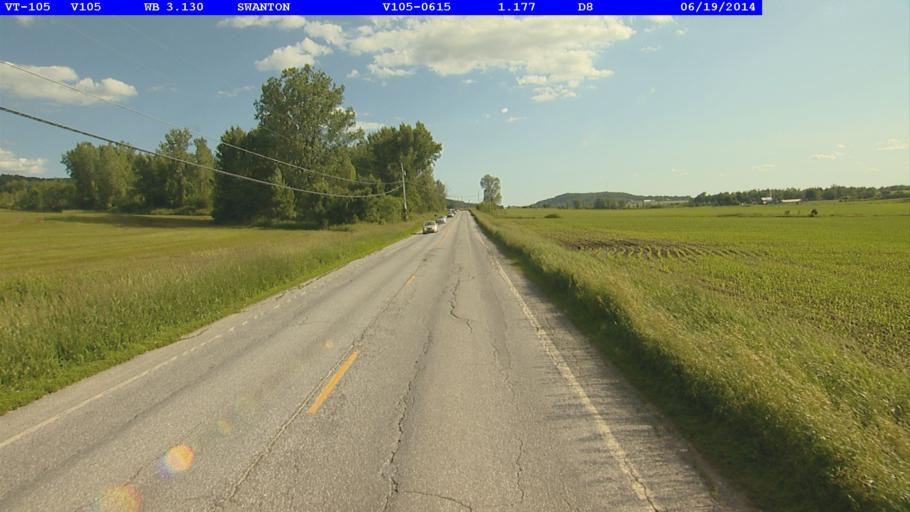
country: US
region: Vermont
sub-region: Franklin County
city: Saint Albans
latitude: 44.8500
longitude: -73.0375
